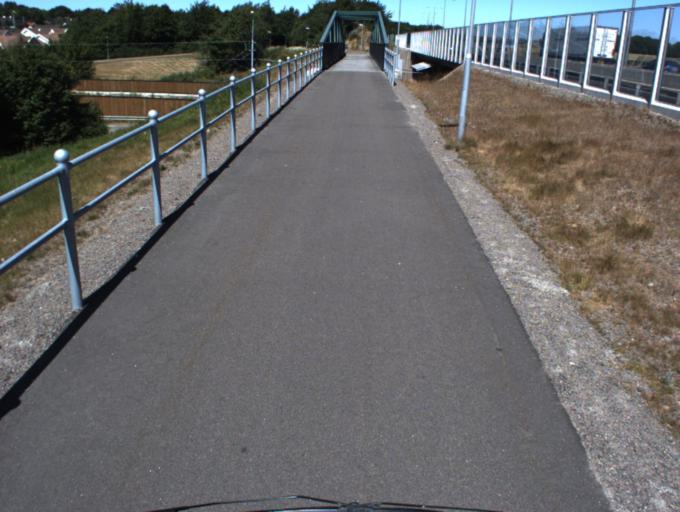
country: SE
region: Skane
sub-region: Helsingborg
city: Gantofta
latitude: 56.0204
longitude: 12.7609
